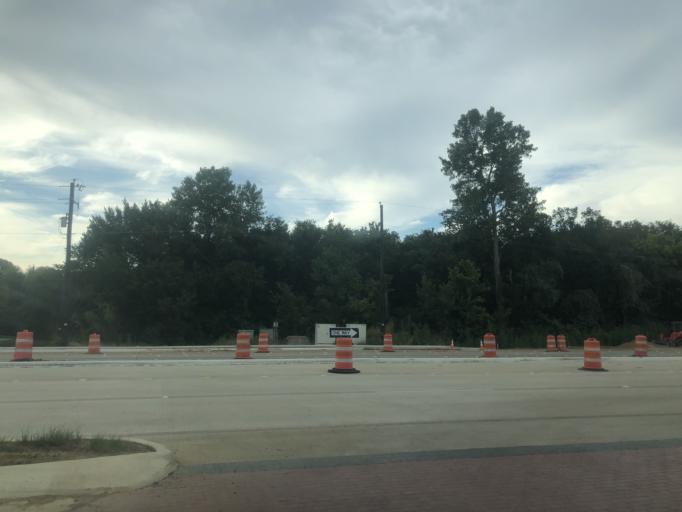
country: US
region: Texas
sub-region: Tarrant County
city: Colleyville
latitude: 32.8771
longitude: -97.1606
